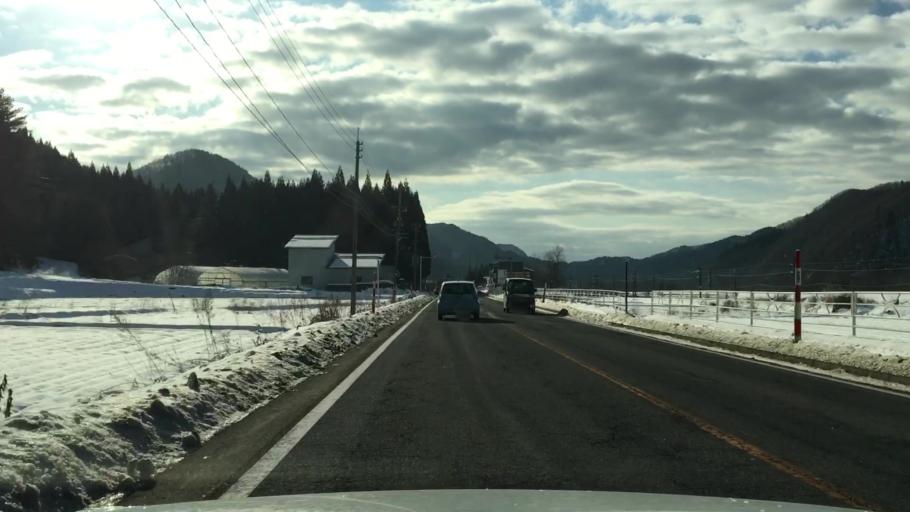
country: JP
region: Akita
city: Odate
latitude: 40.3596
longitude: 140.5974
